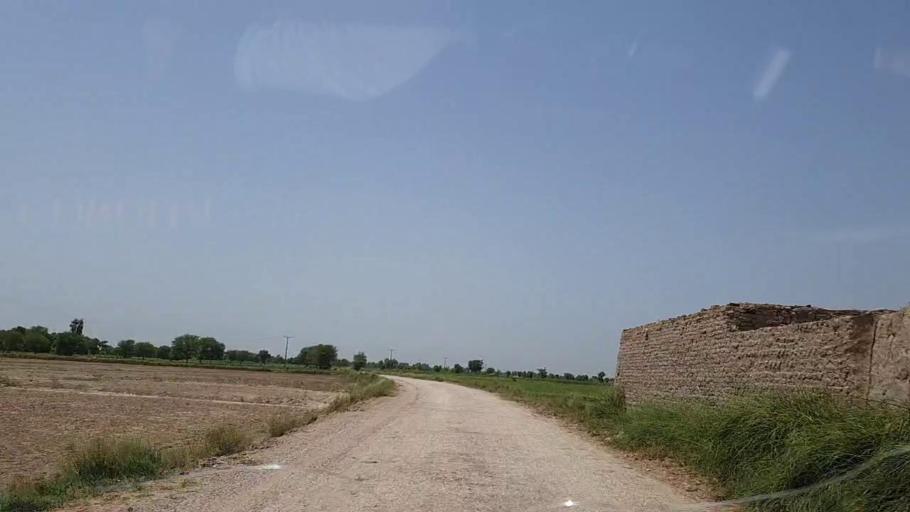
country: PK
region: Sindh
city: Tharu Shah
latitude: 26.9263
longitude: 68.0554
